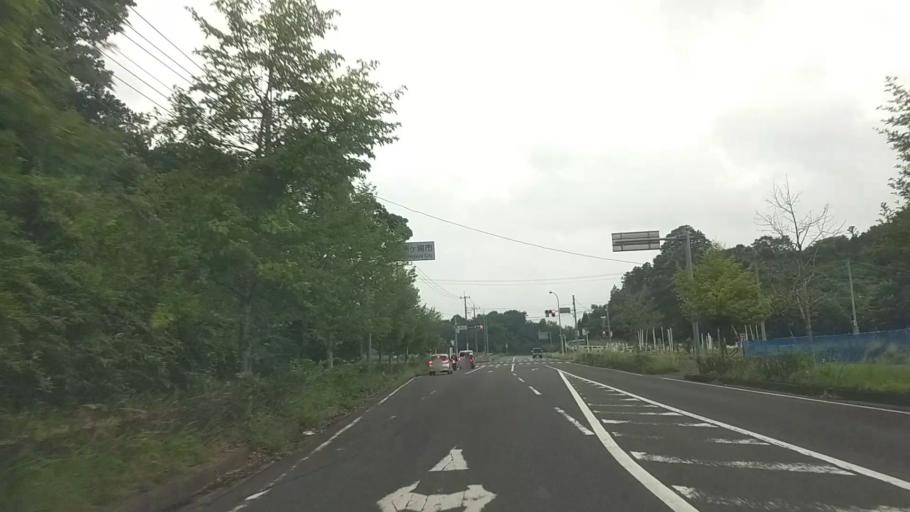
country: JP
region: Chiba
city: Kisarazu
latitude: 35.3854
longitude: 140.0036
